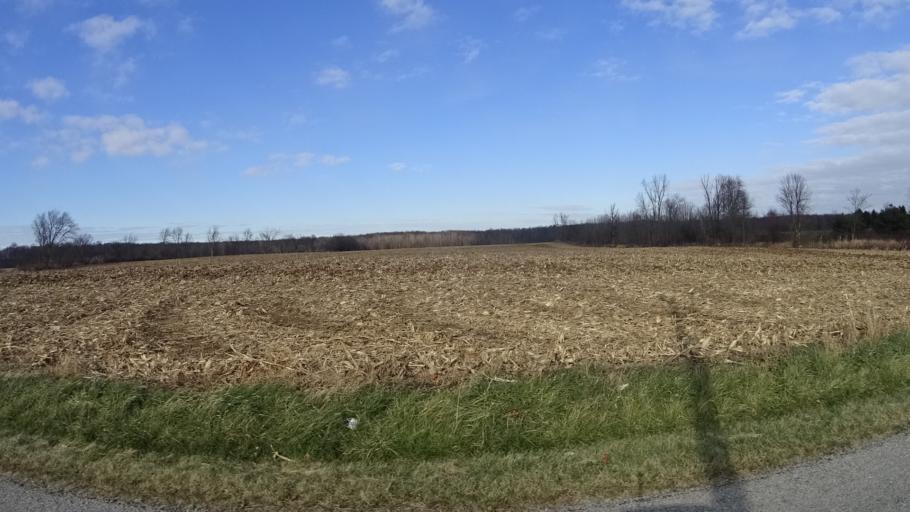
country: US
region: Ohio
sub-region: Lorain County
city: Wellington
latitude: 41.1487
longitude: -82.2831
